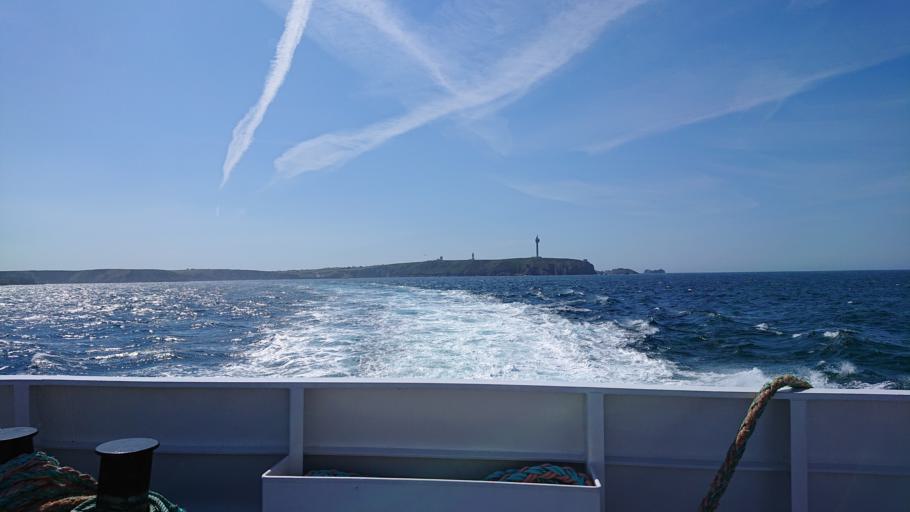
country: FR
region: Brittany
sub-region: Departement du Finistere
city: Porspoder
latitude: 48.4704
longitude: -5.0266
